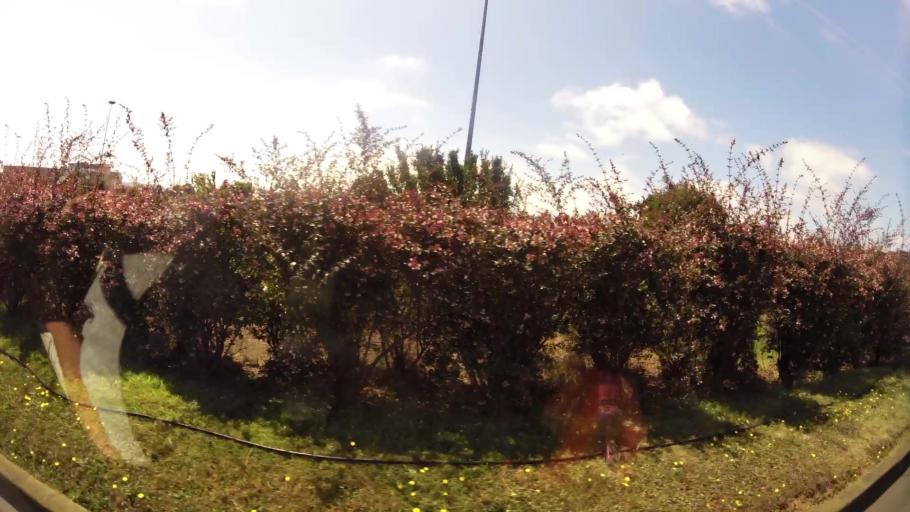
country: CL
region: Biobio
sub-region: Provincia de Concepcion
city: Concepcion
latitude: -36.7966
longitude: -73.0662
